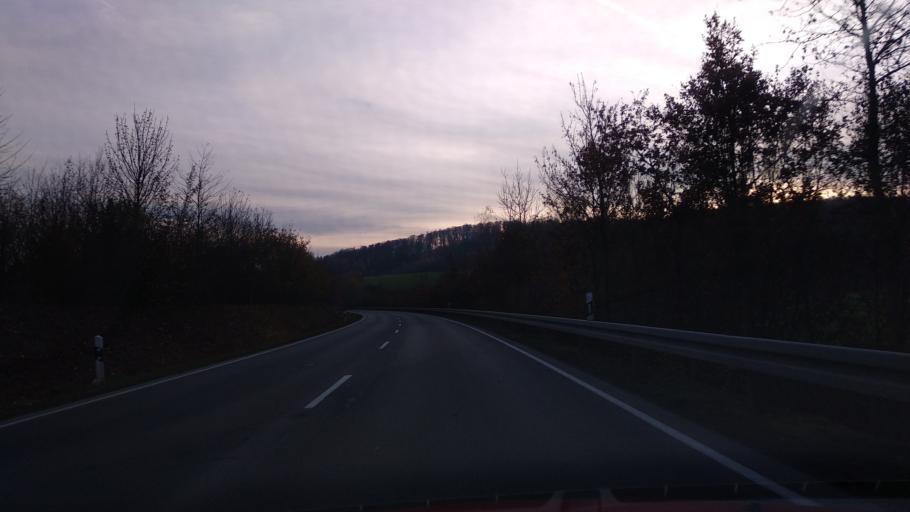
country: DE
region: North Rhine-Westphalia
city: Beverungen
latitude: 51.6951
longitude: 9.3800
